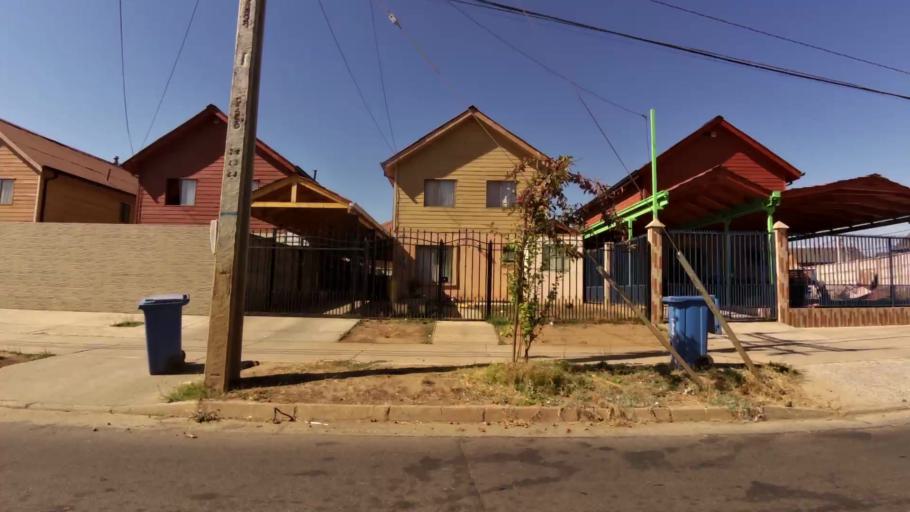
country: CL
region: Maule
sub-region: Provincia de Talca
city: Talca
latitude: -35.4152
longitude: -71.6168
